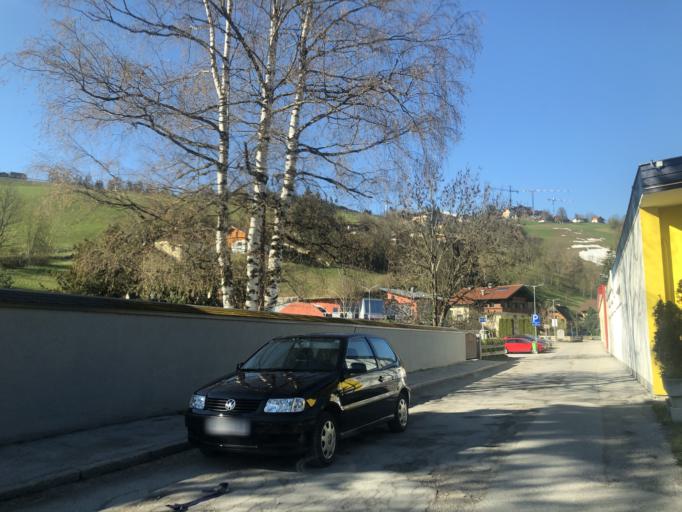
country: AT
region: Styria
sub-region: Politischer Bezirk Liezen
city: Schladming
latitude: 47.3911
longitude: 13.6827
